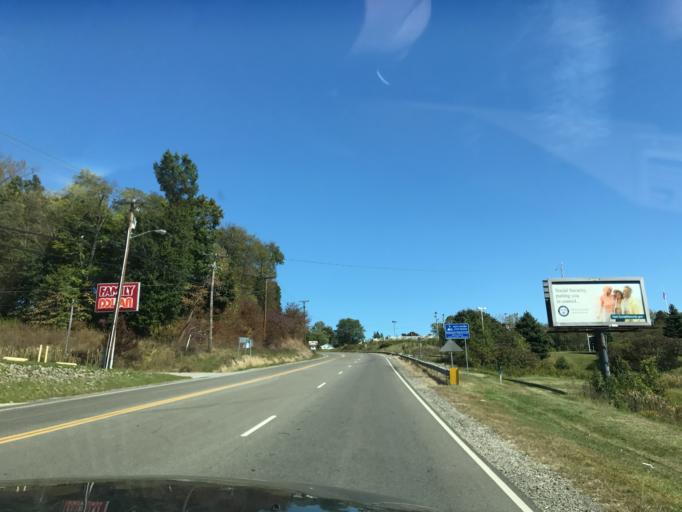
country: US
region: Ohio
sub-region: Muskingum County
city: Pleasant Grove
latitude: 39.9430
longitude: -81.9798
